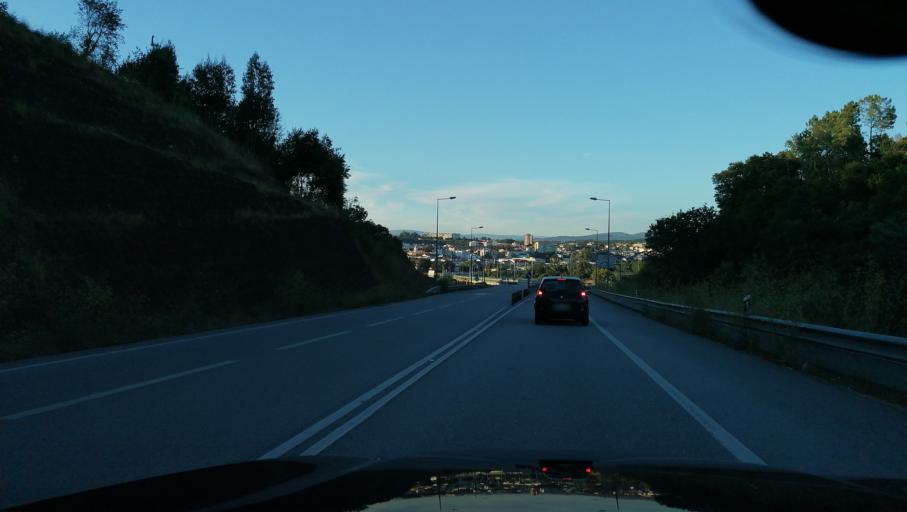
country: PT
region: Aveiro
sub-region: Agueda
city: Agueda
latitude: 40.5630
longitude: -8.4512
